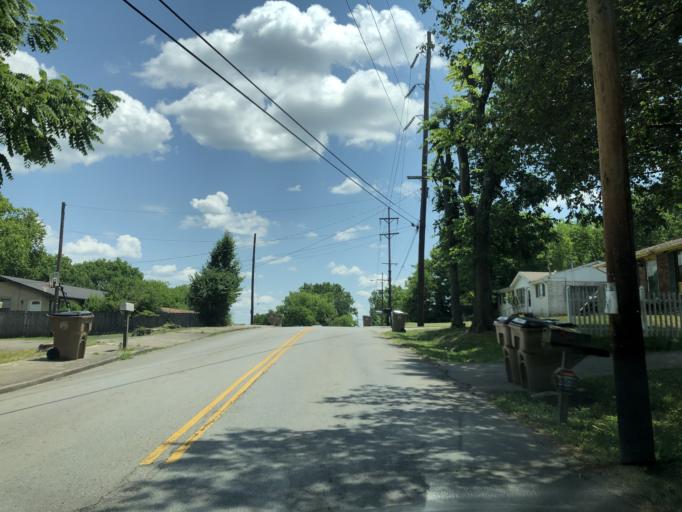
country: US
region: Tennessee
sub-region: Davidson County
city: Goodlettsville
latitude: 36.2728
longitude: -86.6984
